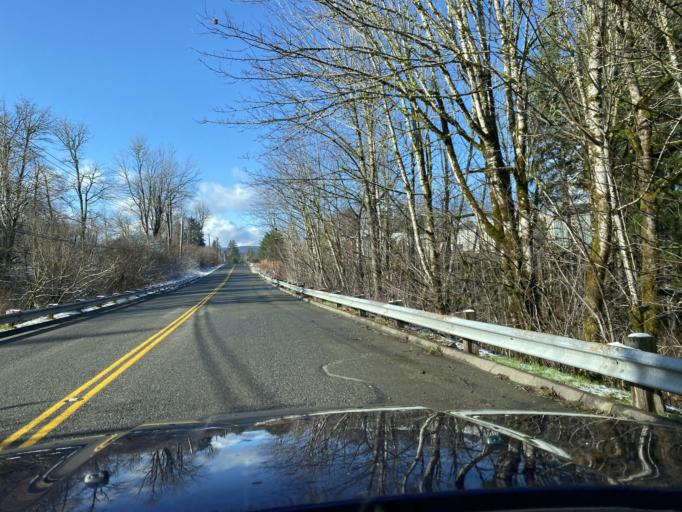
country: US
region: Washington
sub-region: King County
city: Snoqualmie
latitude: 47.5145
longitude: -121.8757
